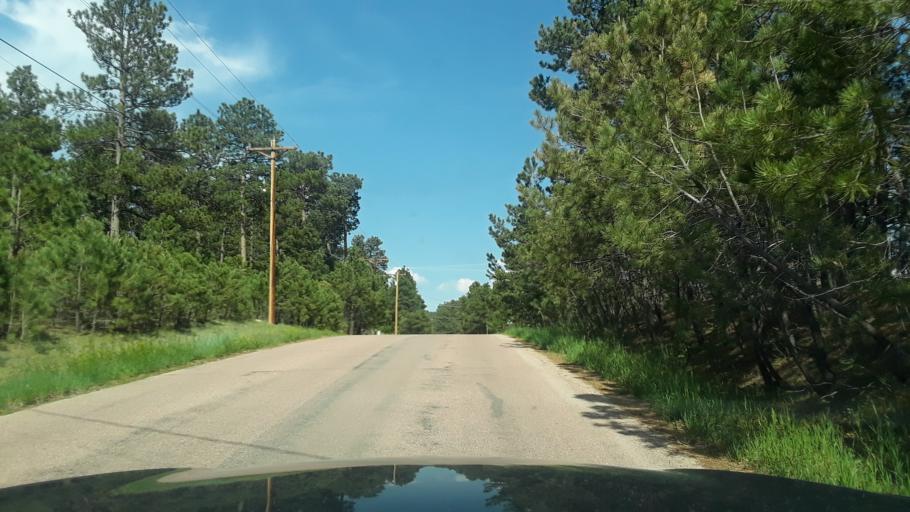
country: US
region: Colorado
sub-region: El Paso County
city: Gleneagle
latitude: 39.0565
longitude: -104.7884
